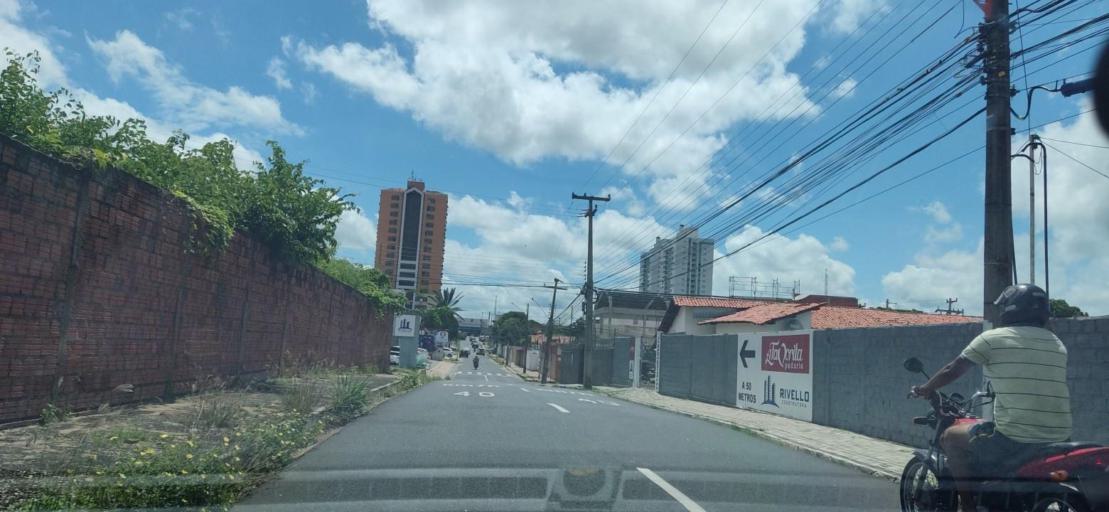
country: BR
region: Piaui
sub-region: Teresina
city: Teresina
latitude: -5.0660
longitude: -42.7732
